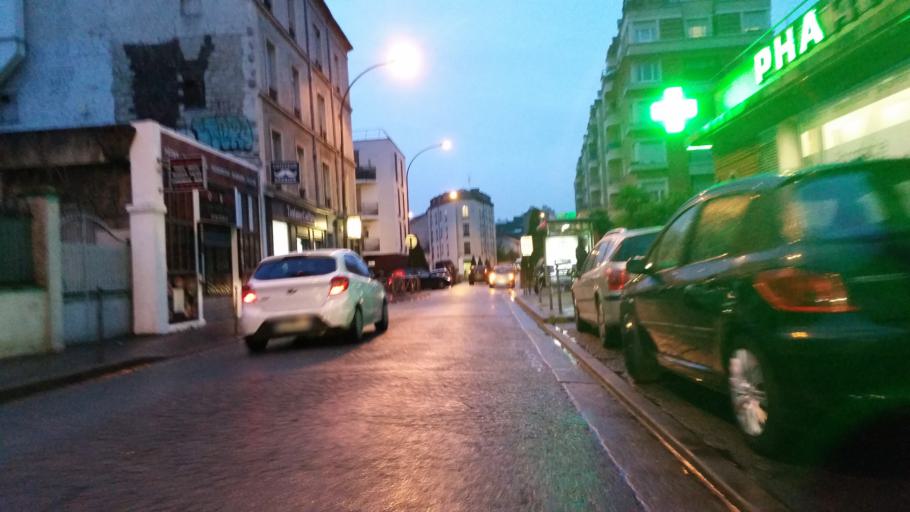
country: FR
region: Ile-de-France
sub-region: Departement du Val-de-Marne
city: Ivry-sur-Seine
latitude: 48.8084
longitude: 2.3878
